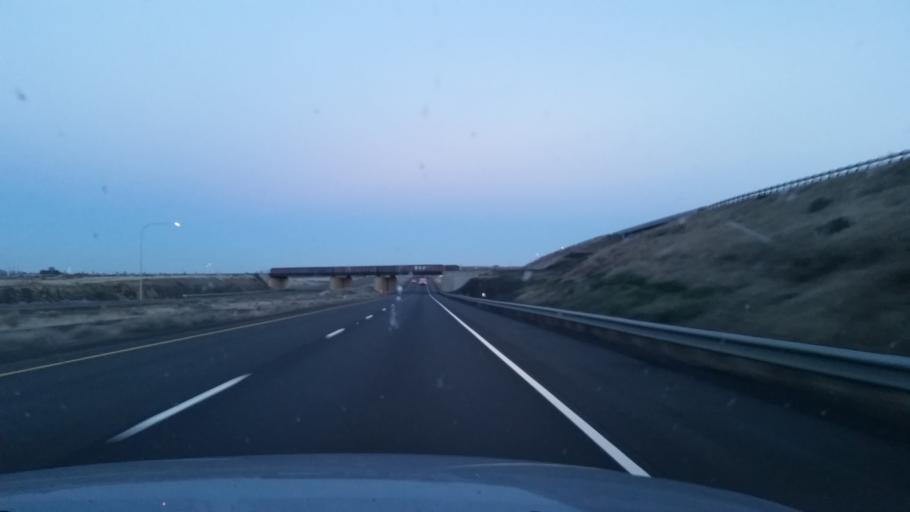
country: US
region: Washington
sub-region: Adams County
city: Ritzville
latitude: 47.1111
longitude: -118.4027
